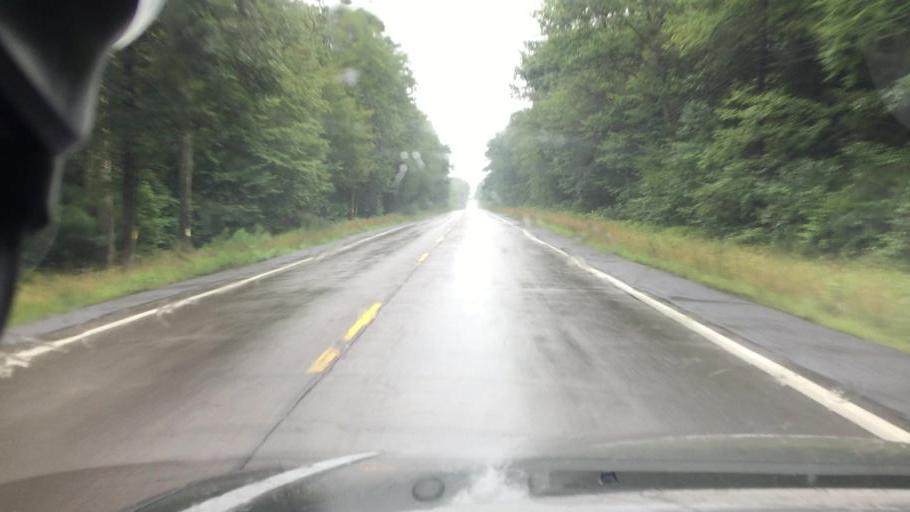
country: US
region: Pennsylvania
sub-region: Luzerne County
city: Freeland
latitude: 41.0313
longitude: -75.8535
